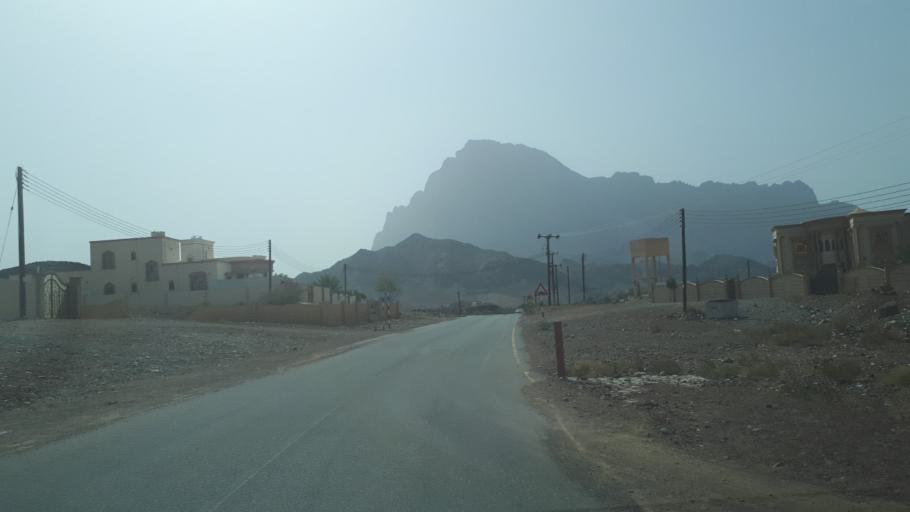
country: OM
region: Muhafazat ad Dakhiliyah
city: Bahla'
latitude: 23.2274
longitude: 57.0475
